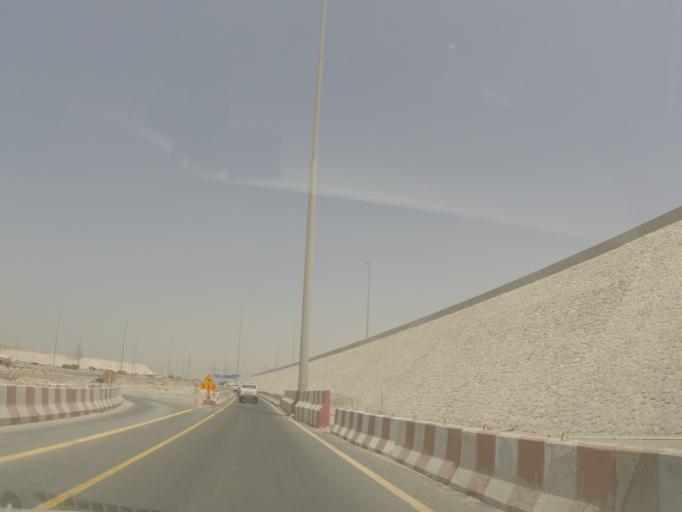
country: AE
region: Dubai
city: Dubai
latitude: 25.0192
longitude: 55.1616
